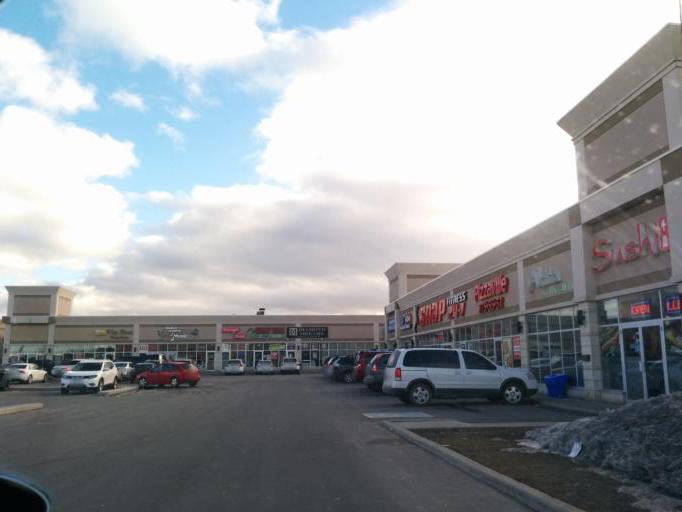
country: CA
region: Ontario
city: Bradford West Gwillimbury
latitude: 44.1089
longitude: -79.5863
